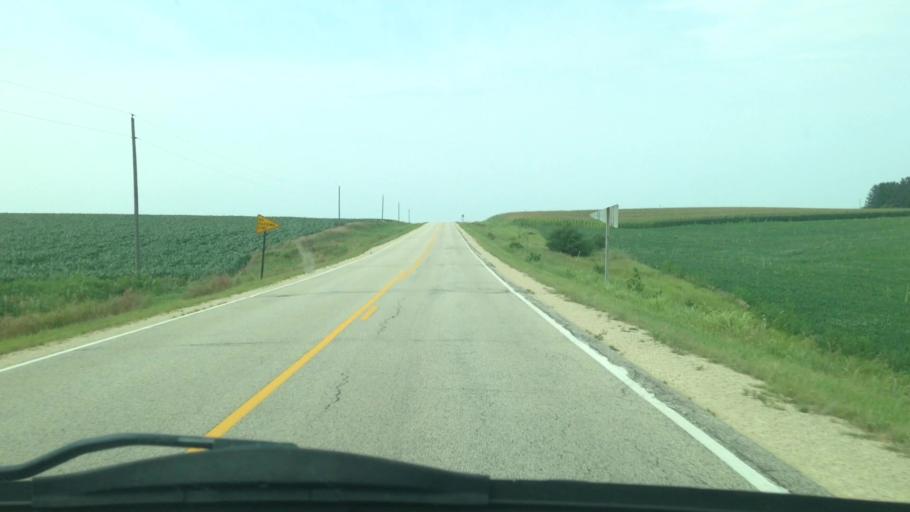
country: US
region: Minnesota
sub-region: Winona County
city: Saint Charles
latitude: 43.8573
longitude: -91.9593
